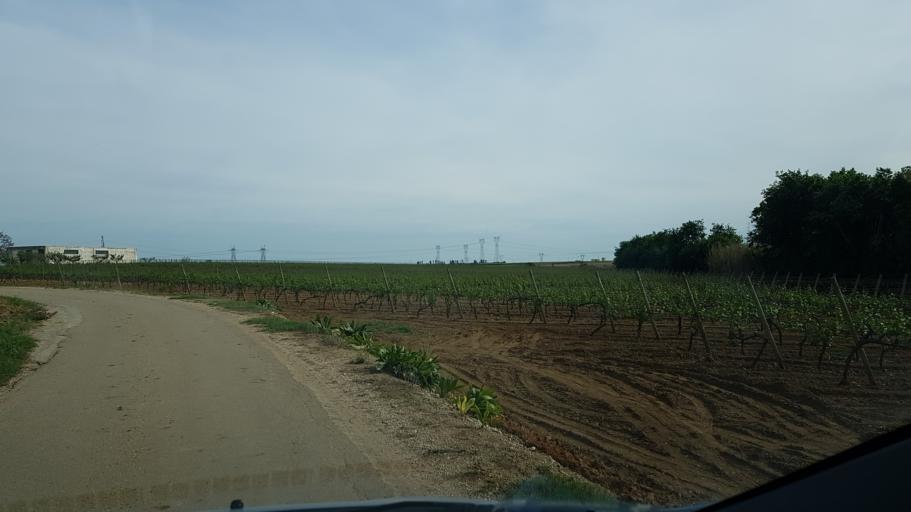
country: IT
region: Apulia
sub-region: Provincia di Brindisi
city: Tuturano
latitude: 40.5605
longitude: 17.9206
